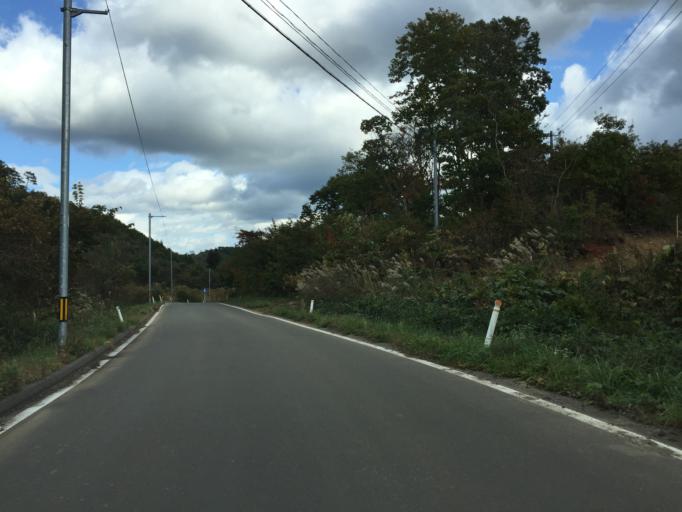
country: JP
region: Miyagi
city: Marumori
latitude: 37.8195
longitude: 140.7584
